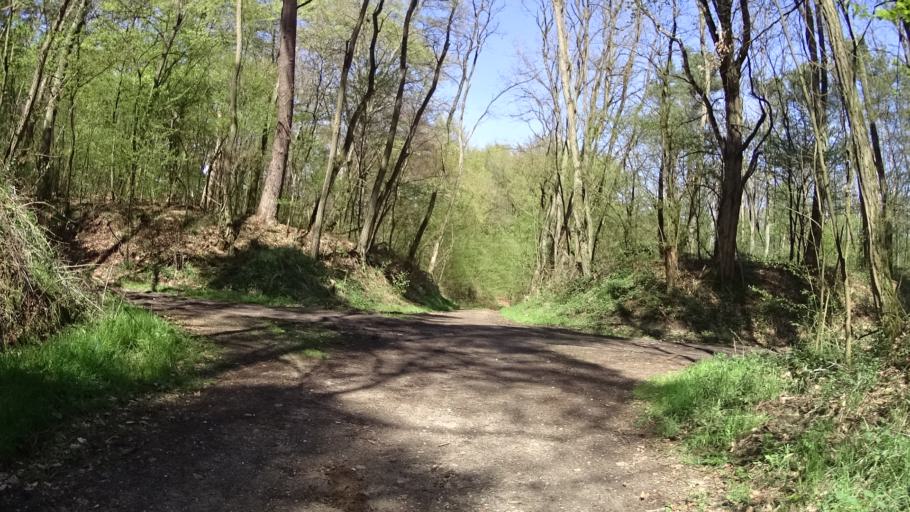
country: DE
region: Hesse
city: Viernheim
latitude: 49.5605
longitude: 8.5868
